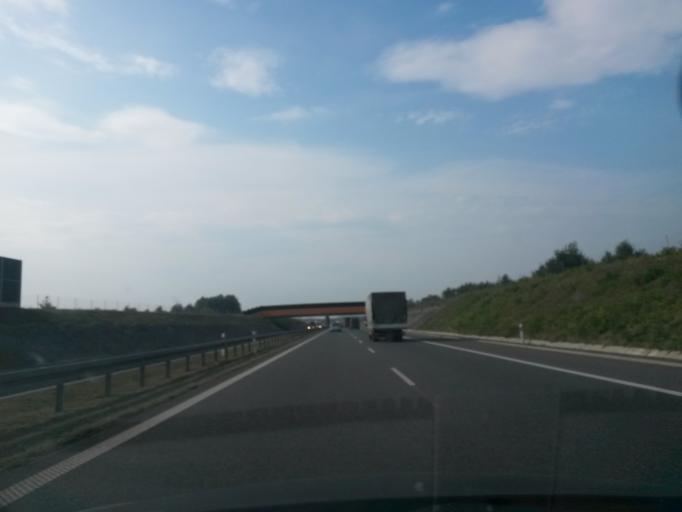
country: PL
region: Lesser Poland Voivodeship
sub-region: Powiat bochenski
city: Jodlowka
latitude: 49.9994
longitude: 20.5547
